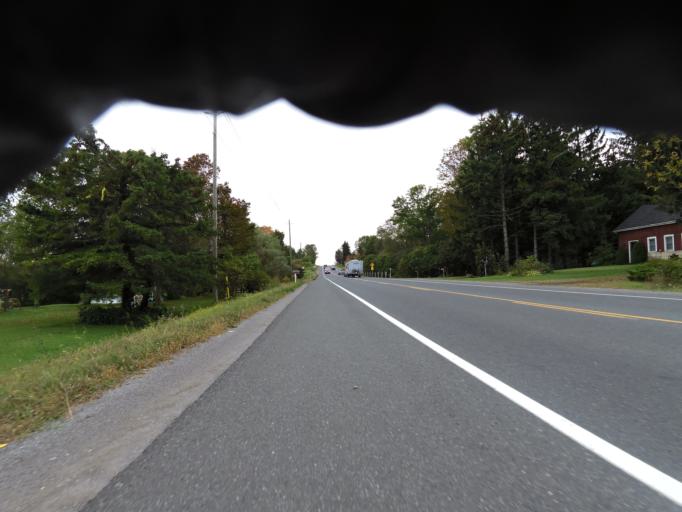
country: CA
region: Ontario
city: Cobourg
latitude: 43.9792
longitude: -78.0825
